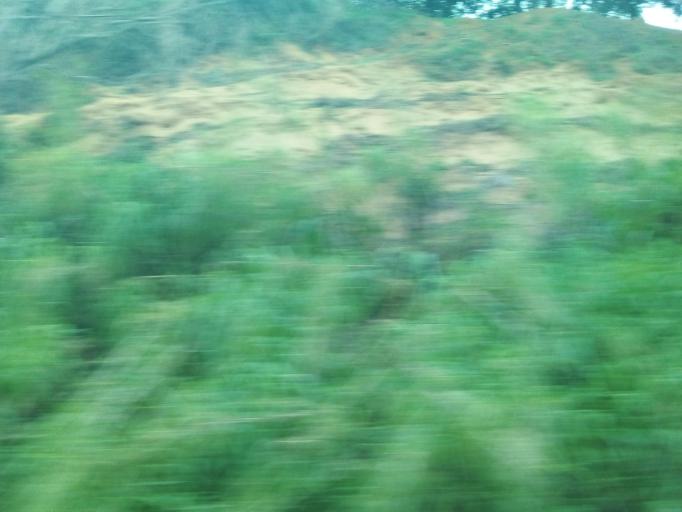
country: BR
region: Minas Gerais
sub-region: Belo Oriente
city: Belo Oriente
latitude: -19.2208
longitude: -42.2998
